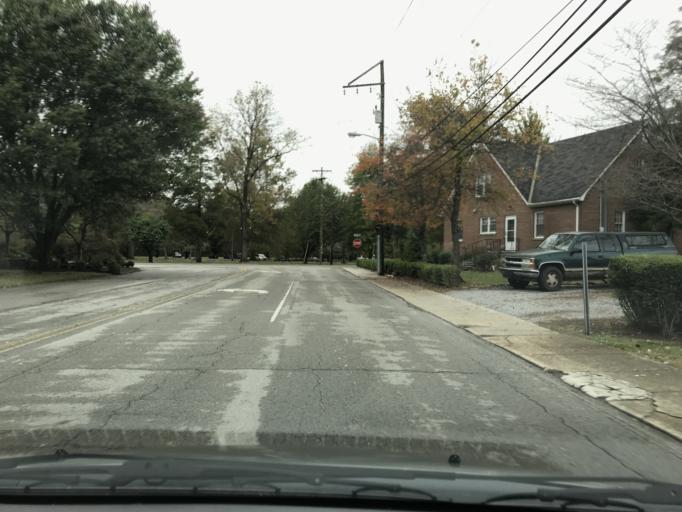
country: US
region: Tennessee
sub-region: Rhea County
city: Dayton
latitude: 35.4862
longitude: -85.0196
